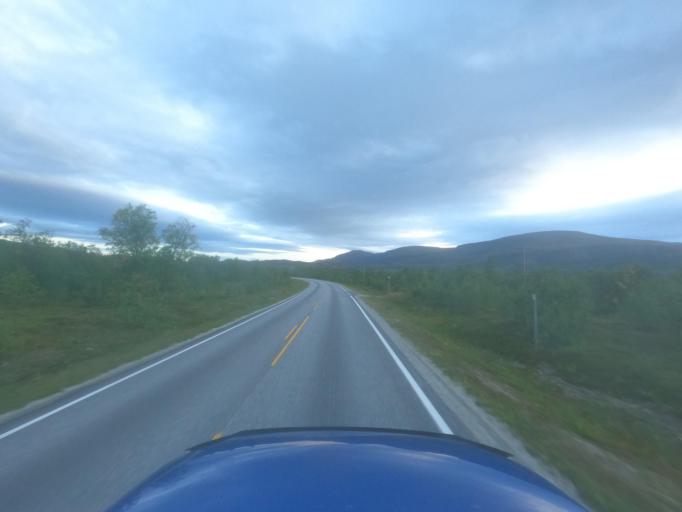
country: NO
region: Finnmark Fylke
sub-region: Porsanger
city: Lakselv
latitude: 69.9568
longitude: 24.9570
